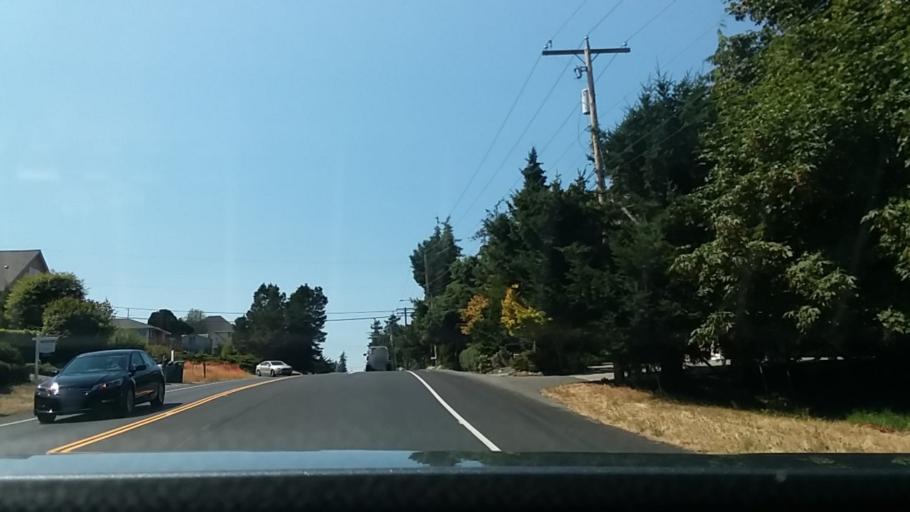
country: US
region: Washington
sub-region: Skagit County
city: Anacortes
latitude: 48.5100
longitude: -122.6467
